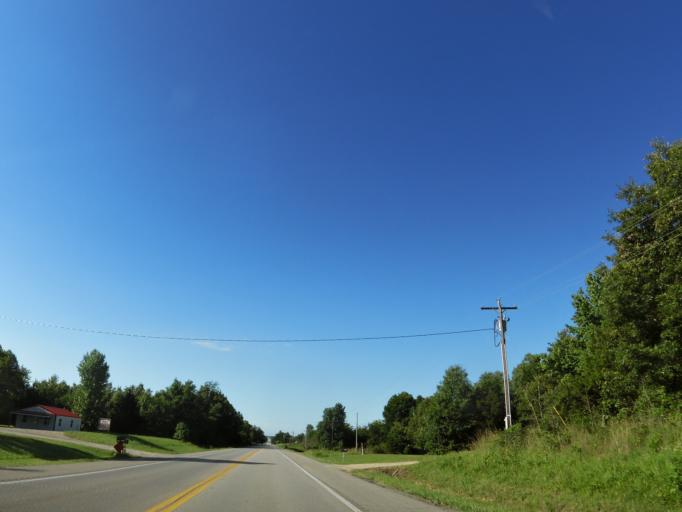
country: US
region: Missouri
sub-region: Butler County
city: Poplar Bluff
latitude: 36.6548
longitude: -90.5202
